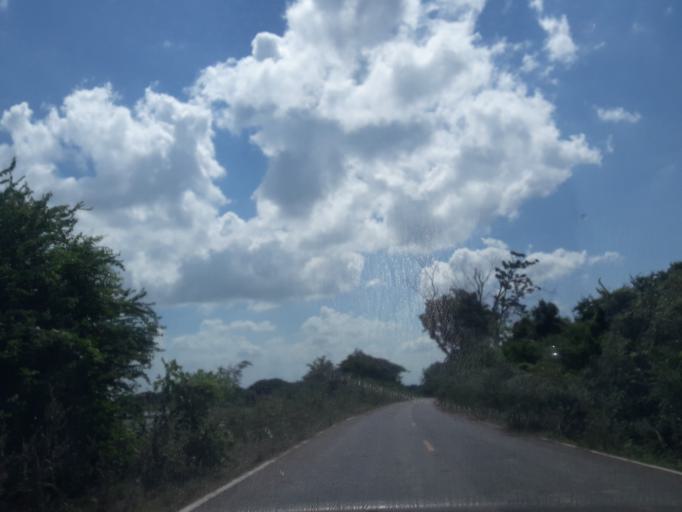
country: TH
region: Lop Buri
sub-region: Amphoe Tha Luang
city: Tha Luang
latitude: 15.0638
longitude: 101.0320
